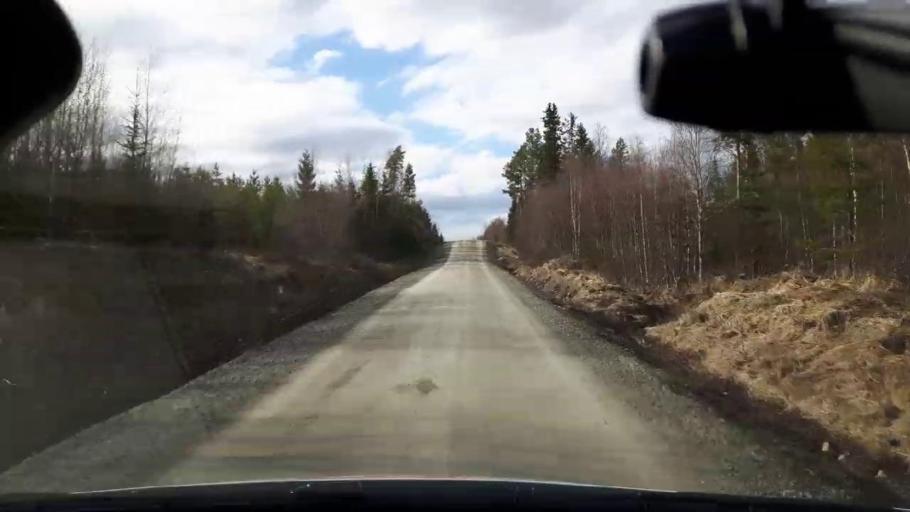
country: SE
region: Jaemtland
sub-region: Bergs Kommun
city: Hoverberg
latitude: 62.8966
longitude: 14.6495
